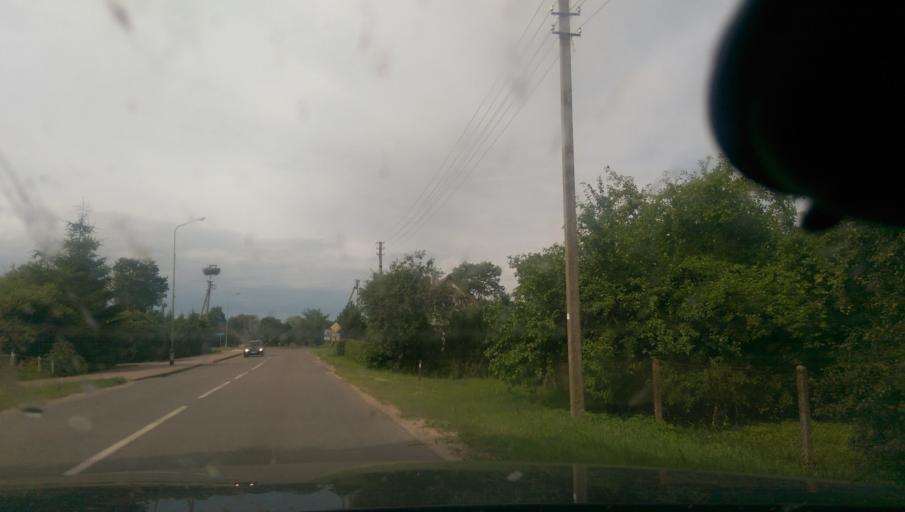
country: LT
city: Rusne
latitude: 55.3005
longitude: 21.3746
